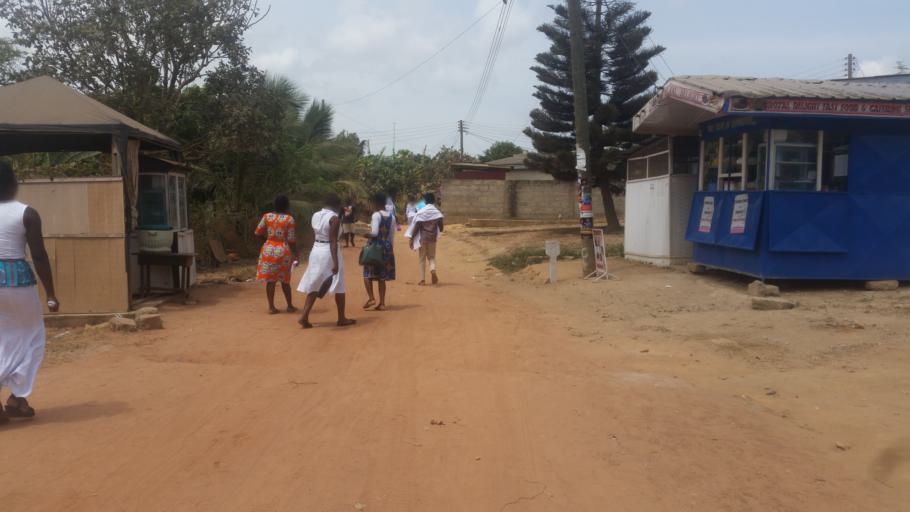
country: GH
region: Central
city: Cape Coast
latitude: 5.1255
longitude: -1.2967
